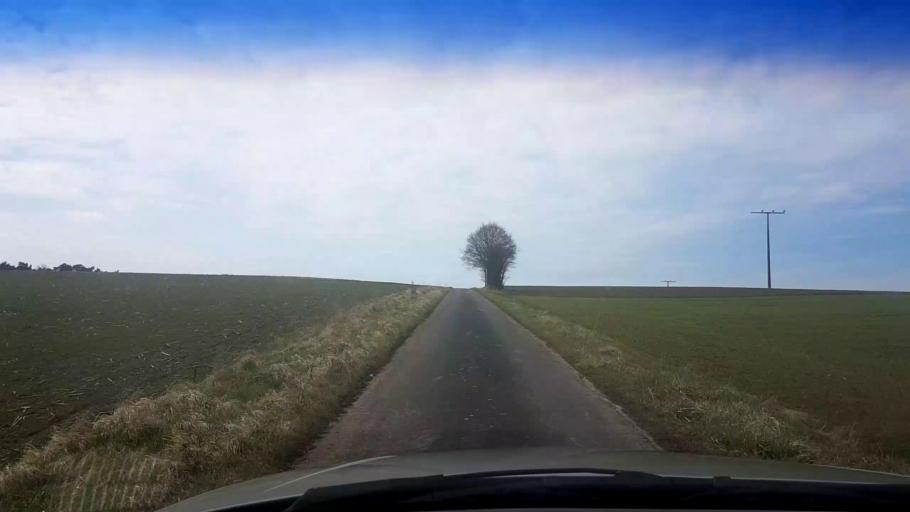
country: DE
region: Bavaria
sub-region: Upper Franconia
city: Burgebrach
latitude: 49.8002
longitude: 10.7587
